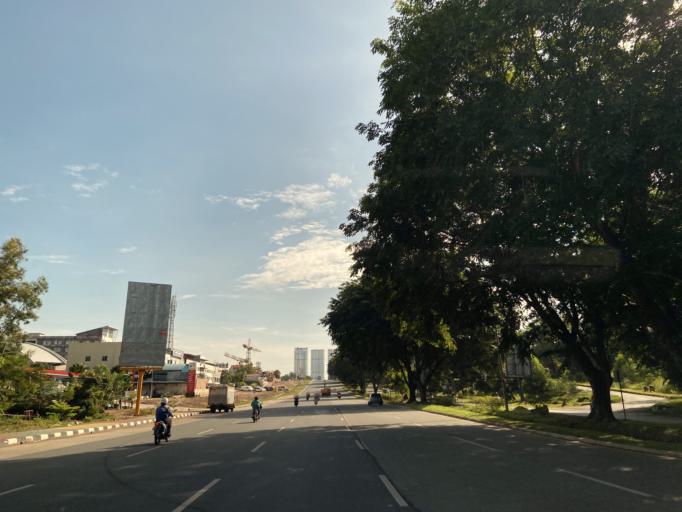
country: SG
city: Singapore
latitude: 1.1038
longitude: 104.0393
